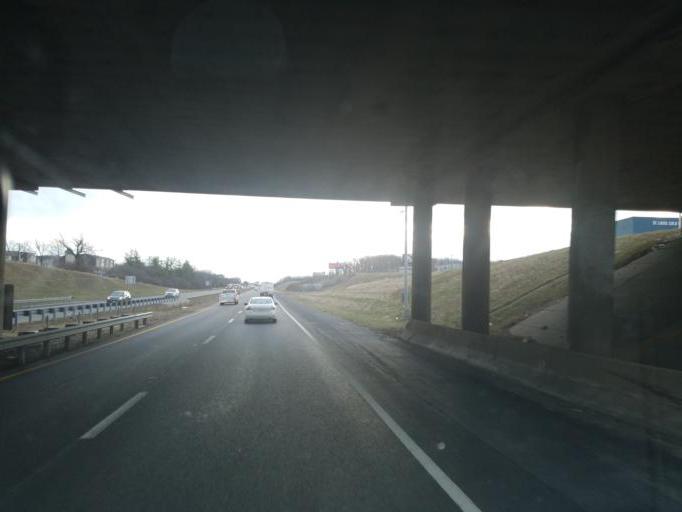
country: US
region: Missouri
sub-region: Saint Louis County
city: Glasgow Village
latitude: 38.7671
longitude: -90.2032
